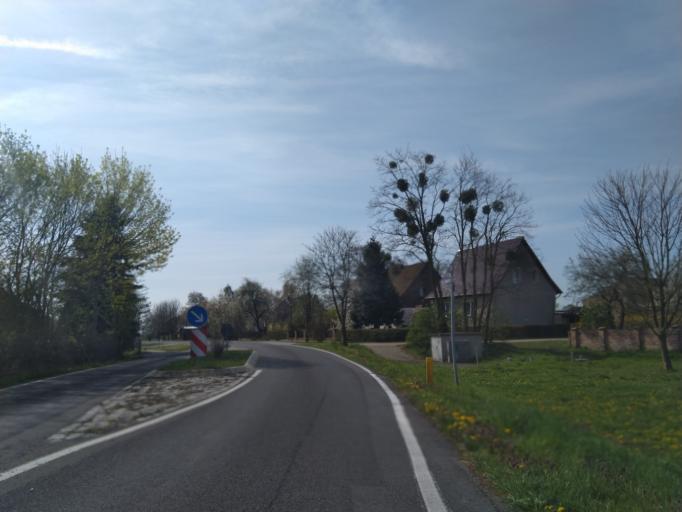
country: DE
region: Brandenburg
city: Wriezen
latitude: 52.7308
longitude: 14.1675
